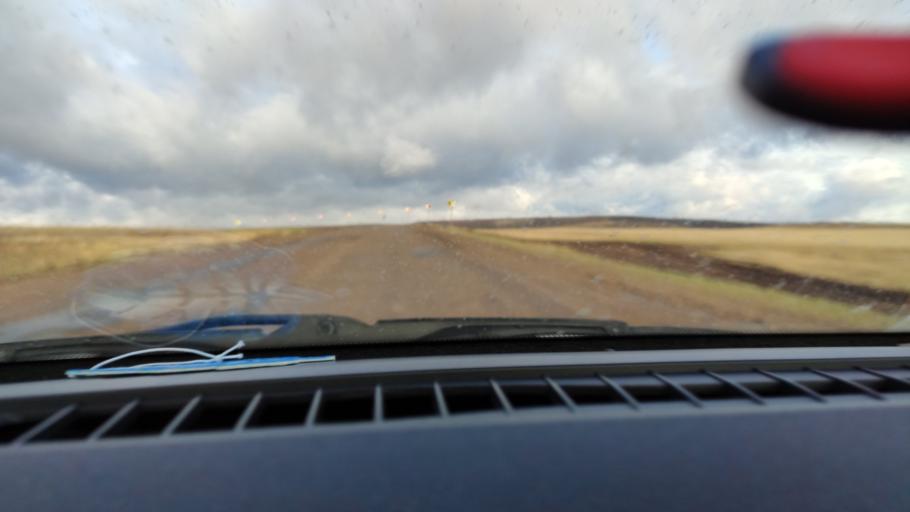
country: RU
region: Tatarstan
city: Russkiy Aktash
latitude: 55.0391
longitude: 52.0325
